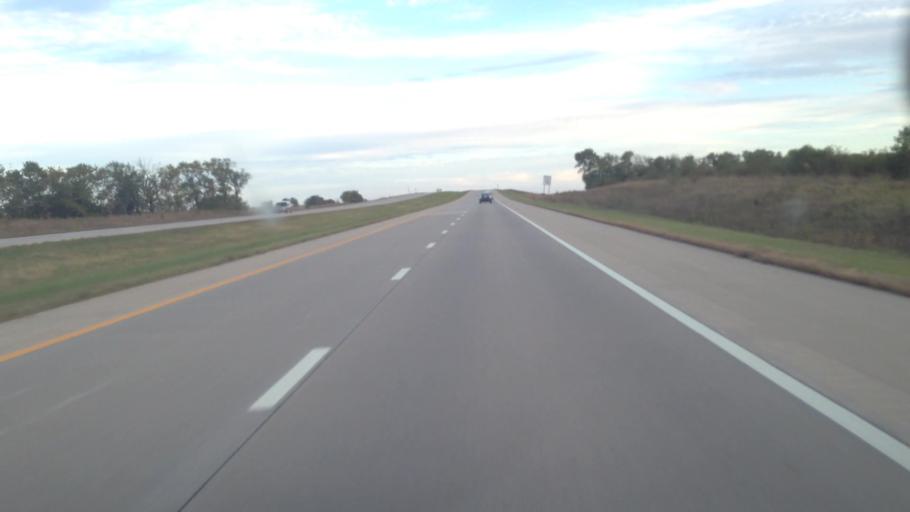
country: US
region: Kansas
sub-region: Franklin County
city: Ottawa
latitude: 38.6584
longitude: -95.2419
